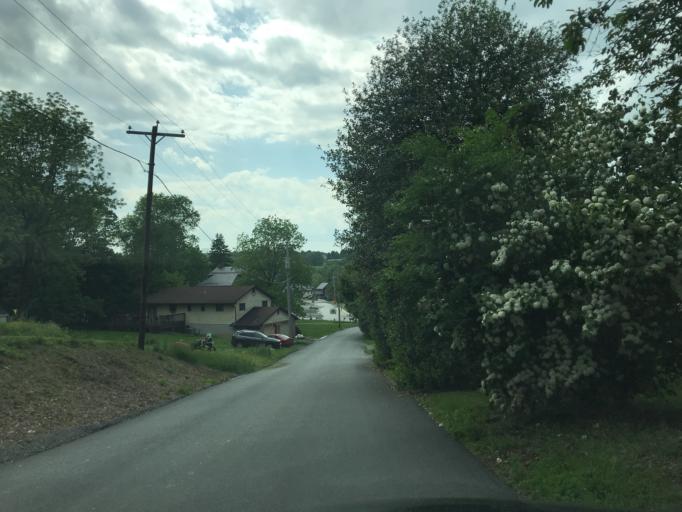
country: US
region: Pennsylvania
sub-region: York County
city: Susquehanna Trails
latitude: 39.7217
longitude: -76.3332
